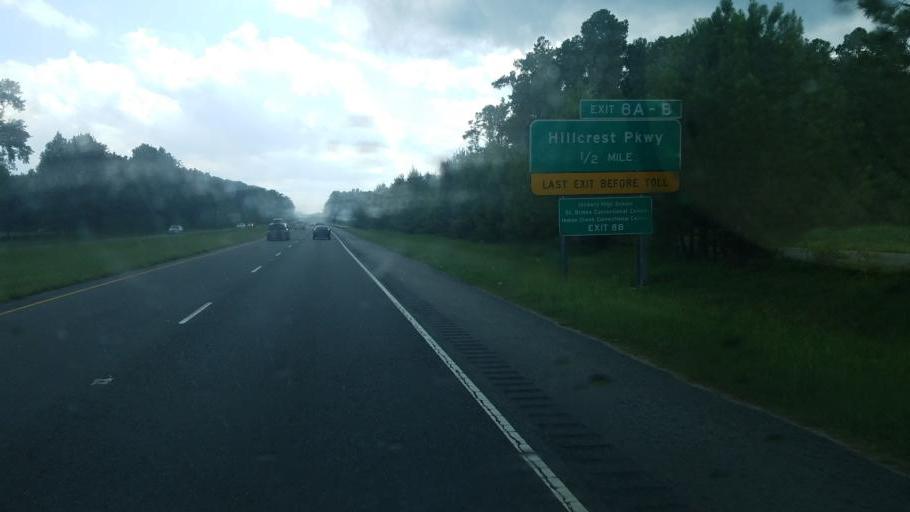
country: US
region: North Carolina
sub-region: Currituck County
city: Moyock
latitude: 36.6703
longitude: -76.2306
